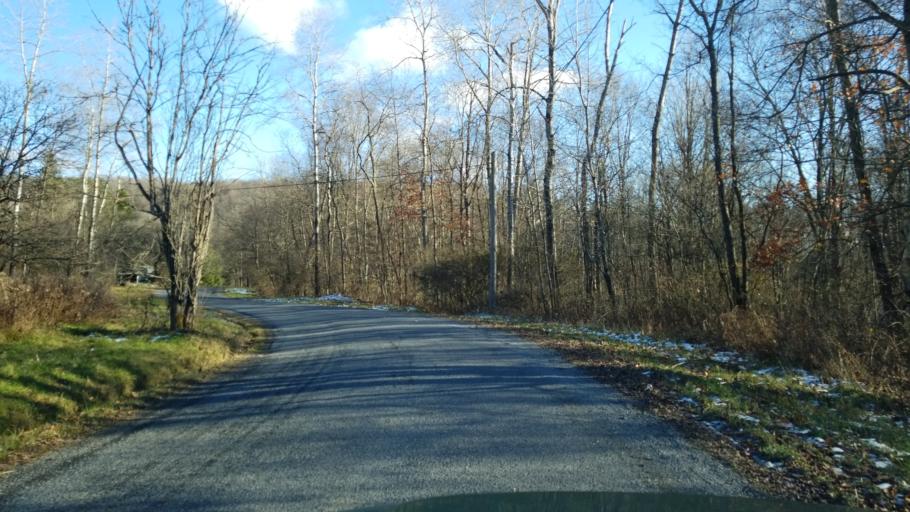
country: US
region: Pennsylvania
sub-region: Jefferson County
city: Brockway
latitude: 41.2598
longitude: -78.8010
